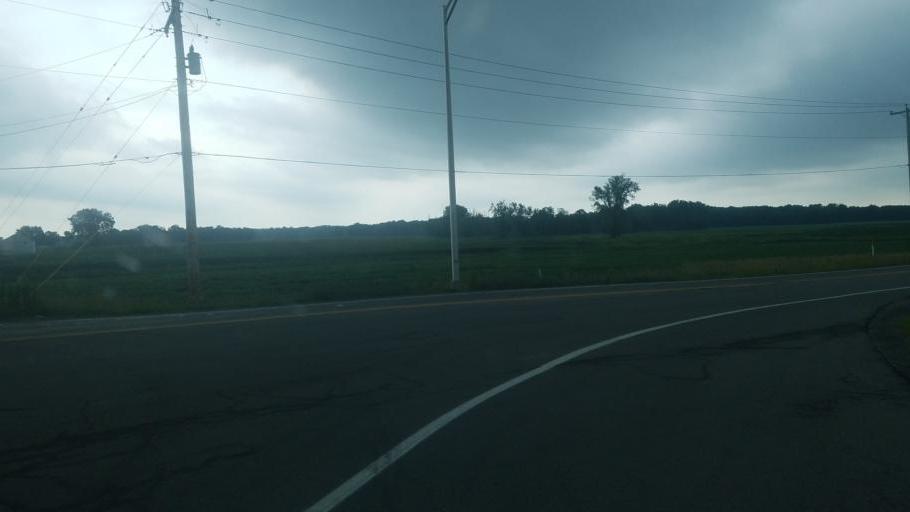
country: US
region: Ohio
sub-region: Logan County
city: Russells Point
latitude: 40.5323
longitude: -83.8331
